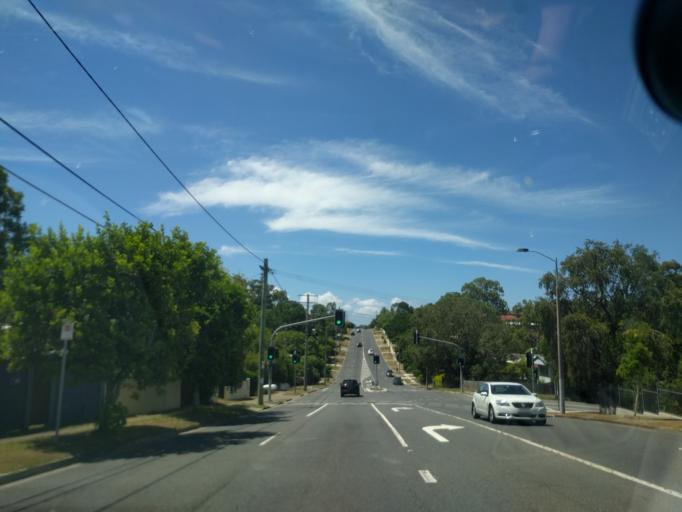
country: AU
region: Queensland
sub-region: Brisbane
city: Stafford Heights
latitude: -27.3971
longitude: 153.0103
